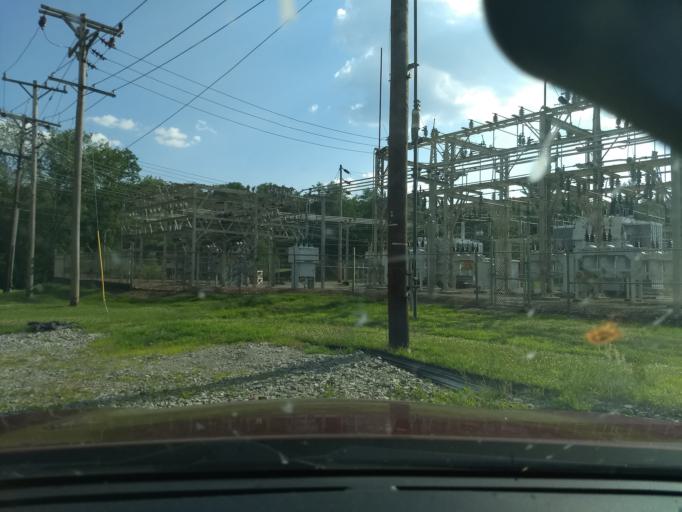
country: US
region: Pennsylvania
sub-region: Westmoreland County
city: Irwin
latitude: 40.3383
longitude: -79.7210
